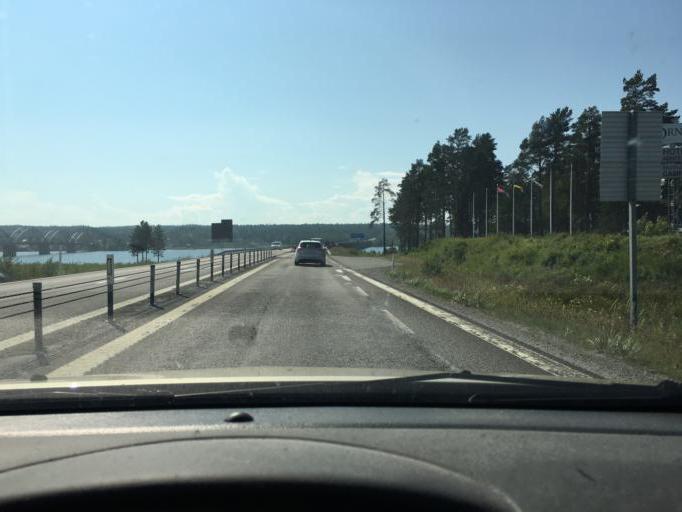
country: SE
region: Norrbotten
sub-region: Lulea Kommun
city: Gammelstad
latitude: 65.5937
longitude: 22.0366
